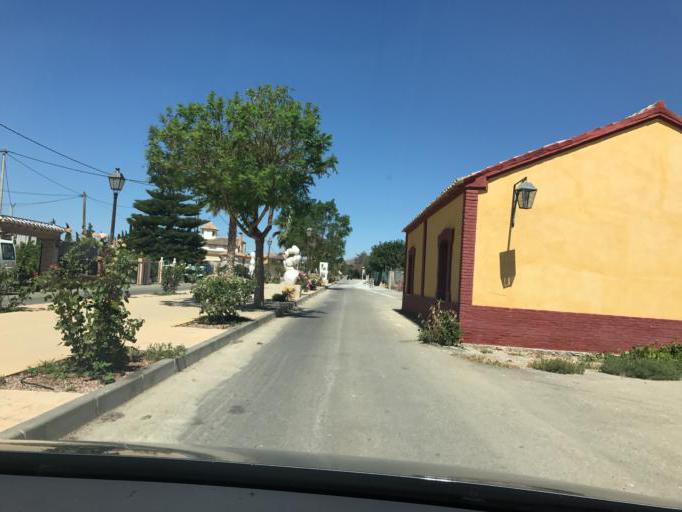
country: ES
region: Andalusia
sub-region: Provincia de Almeria
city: Fines
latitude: 37.3574
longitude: -2.2623
